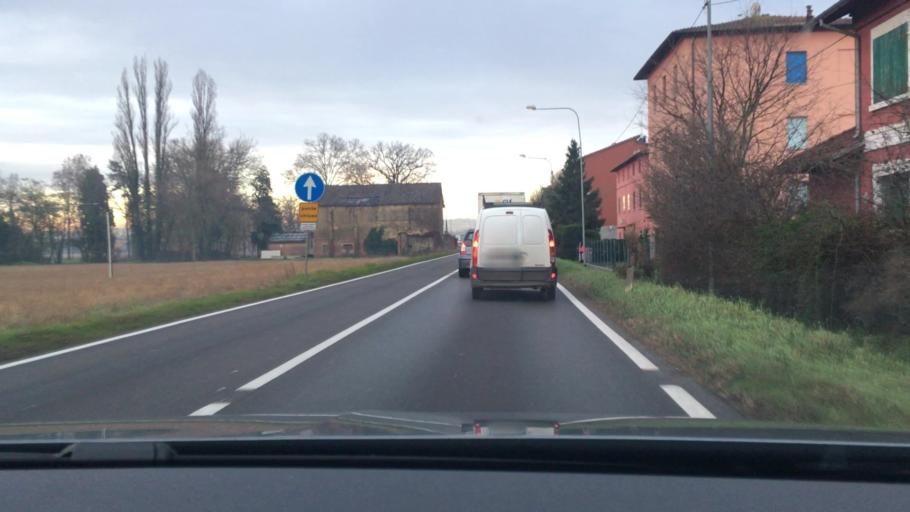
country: IT
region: Emilia-Romagna
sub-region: Provincia di Modena
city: Albareto
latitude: 44.7007
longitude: 10.9497
